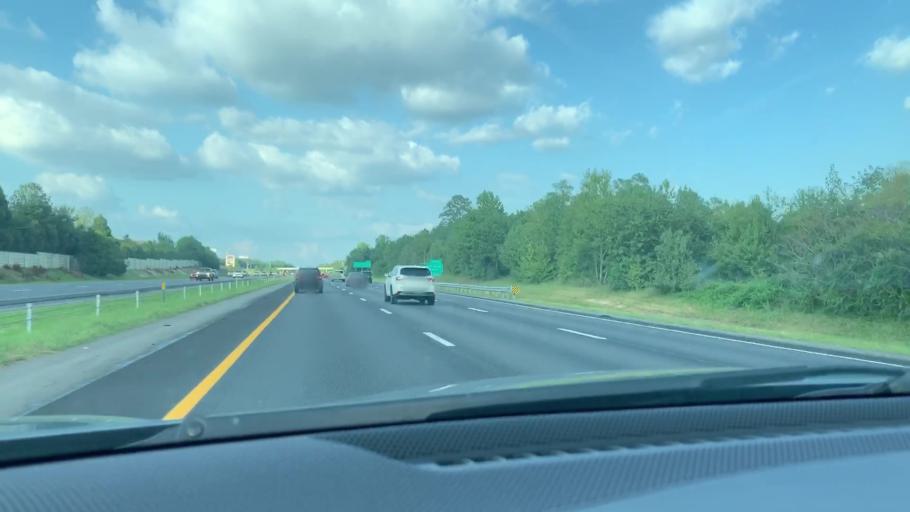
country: US
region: South Carolina
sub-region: Richland County
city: Forest Acres
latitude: 34.0135
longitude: -80.9513
